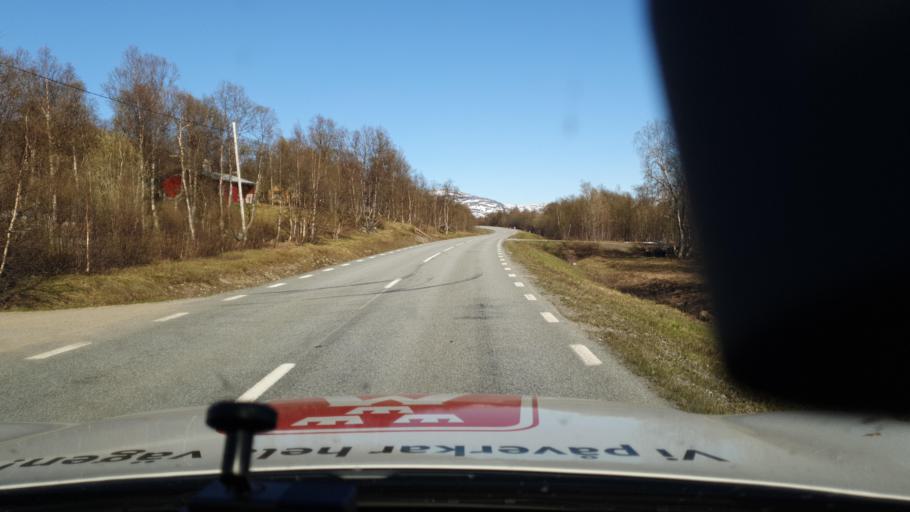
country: NO
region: Nordland
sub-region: Rana
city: Mo i Rana
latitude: 66.0432
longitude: 14.9863
